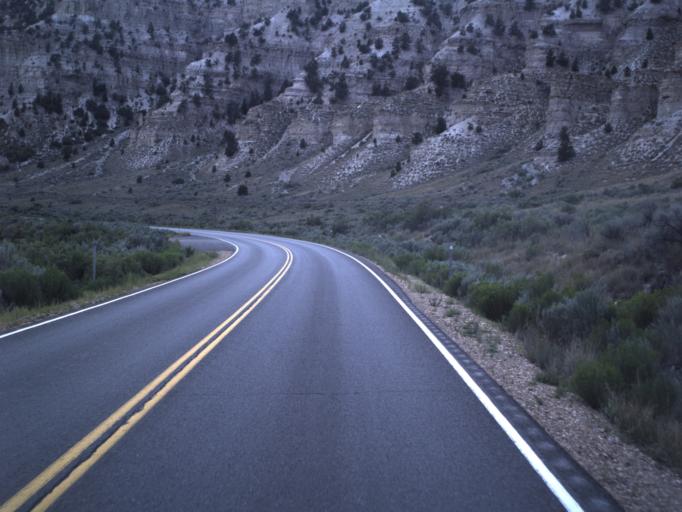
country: US
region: Utah
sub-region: Duchesne County
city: Duchesne
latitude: 40.0464
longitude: -110.5343
